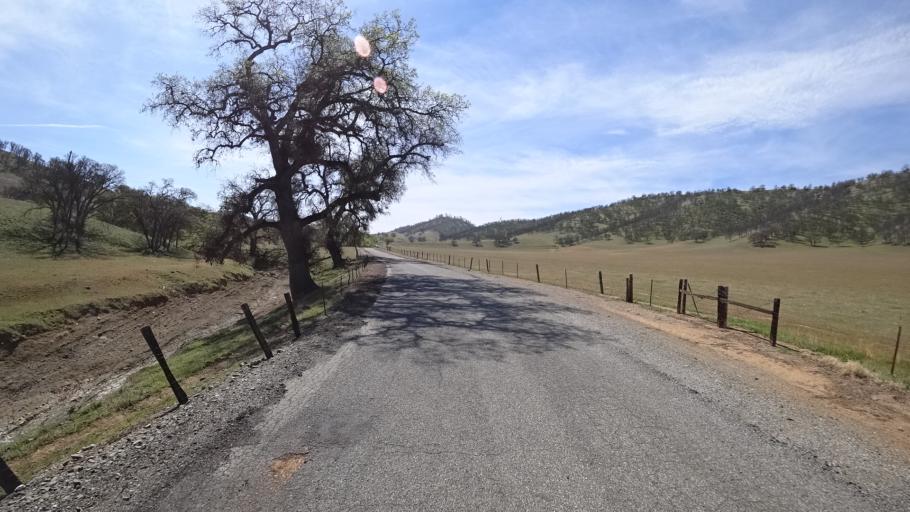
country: US
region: California
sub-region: Glenn County
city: Willows
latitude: 39.5245
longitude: -122.4574
